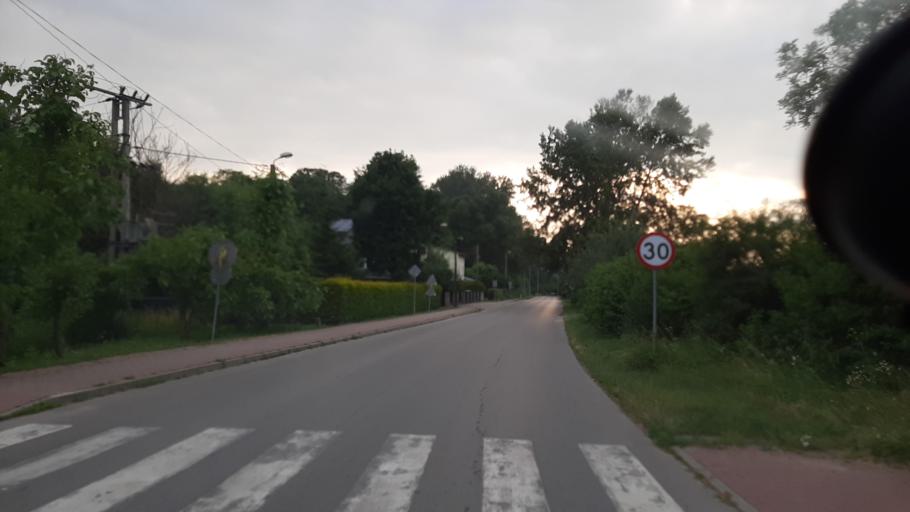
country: PL
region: Lublin Voivodeship
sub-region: Powiat lubelski
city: Garbow
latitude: 51.3495
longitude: 22.3357
